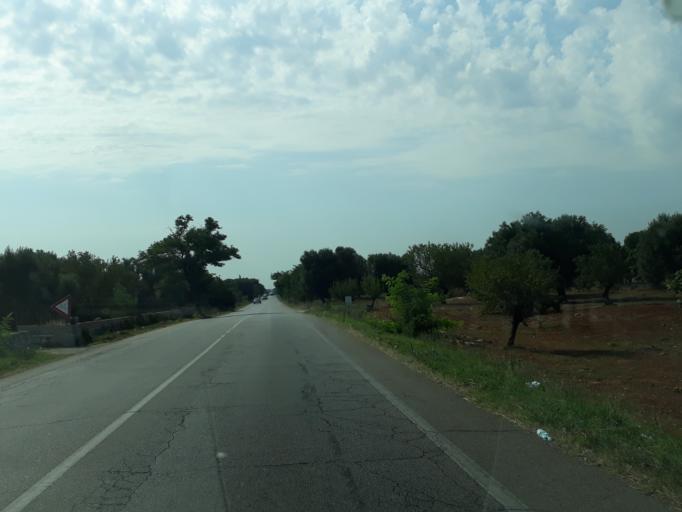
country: IT
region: Apulia
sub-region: Provincia di Brindisi
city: Carovigno
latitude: 40.6911
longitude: 17.6733
